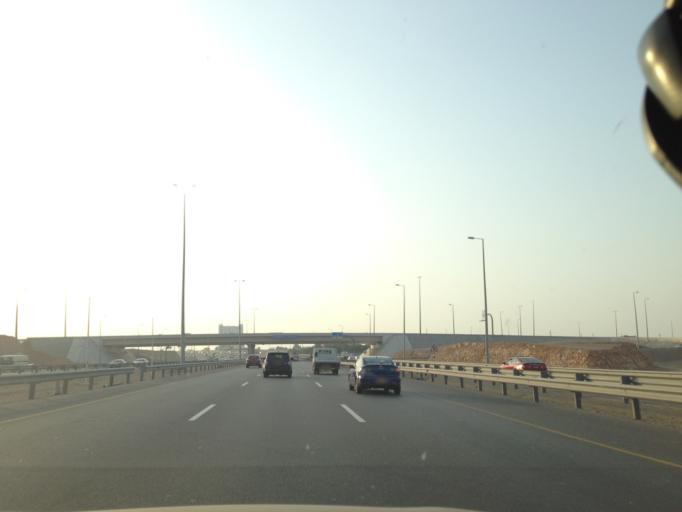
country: OM
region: Muhafazat Masqat
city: Bawshar
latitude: 23.5660
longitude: 58.3816
